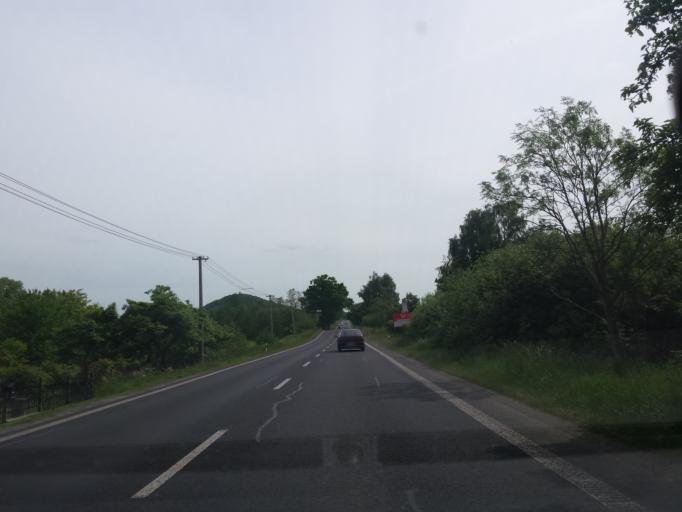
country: CZ
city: Novy Bor
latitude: 50.7227
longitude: 14.5458
